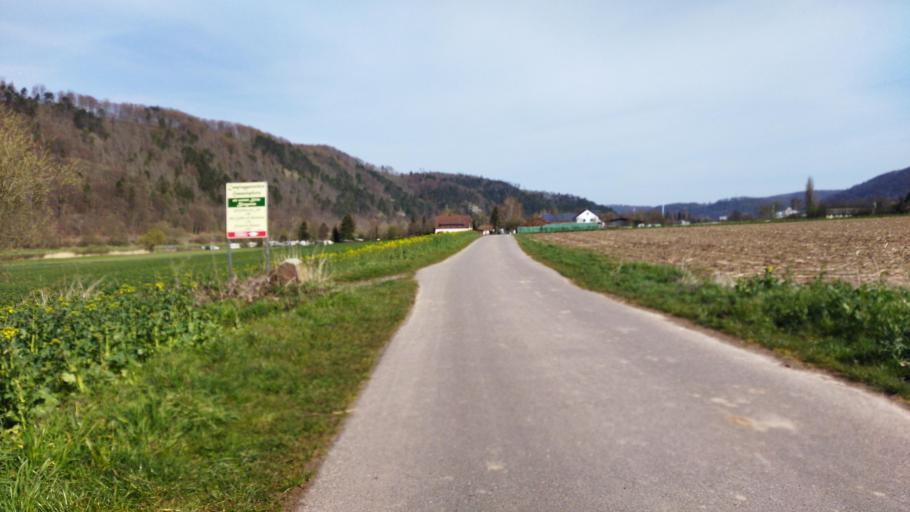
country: DE
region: Lower Saxony
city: Bodenwerder
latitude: 51.9551
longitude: 9.5051
